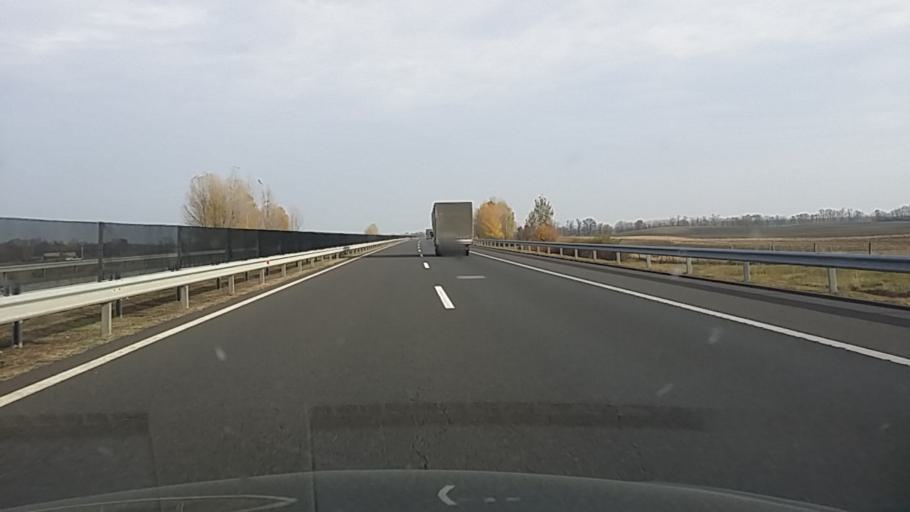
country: HU
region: Szabolcs-Szatmar-Bereg
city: Nagycserkesz
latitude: 47.9025
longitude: 21.5178
